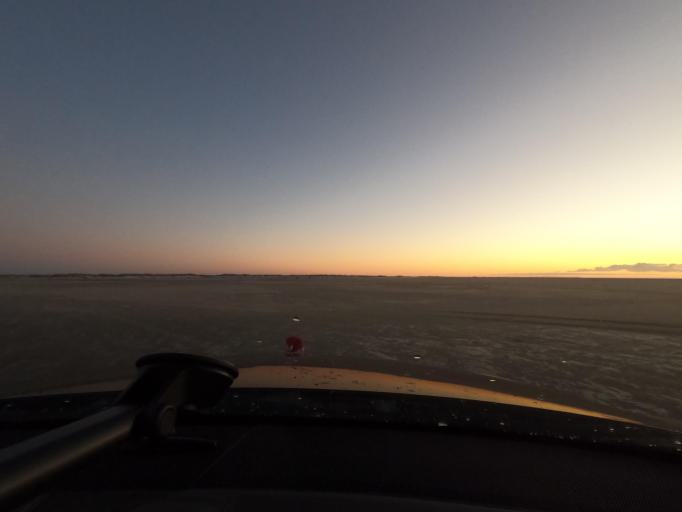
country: DE
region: Schleswig-Holstein
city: List
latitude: 55.1518
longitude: 8.4812
